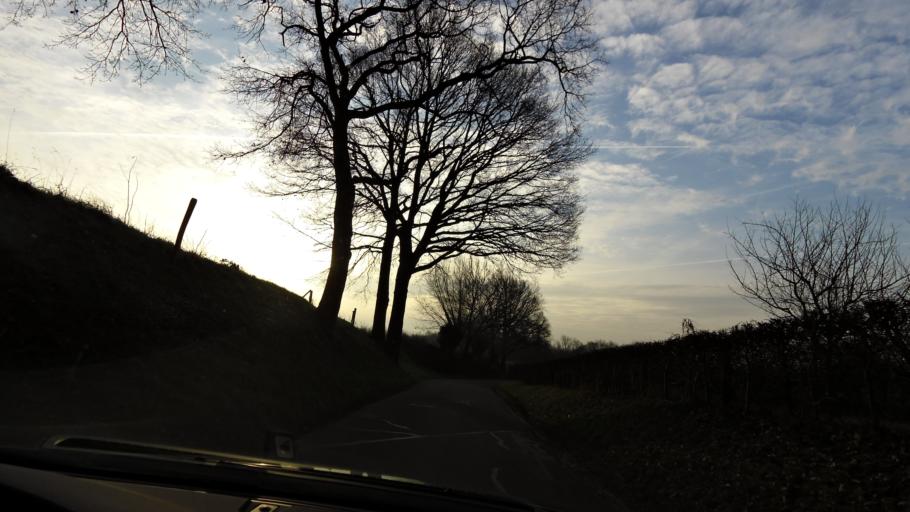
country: NL
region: Limburg
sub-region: Gemeente Nuth
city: Nuth
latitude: 50.9172
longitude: 5.8539
